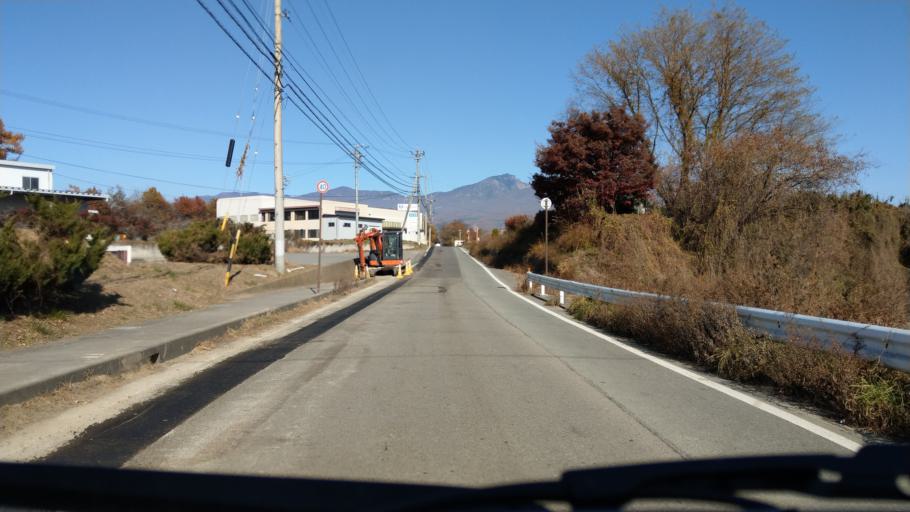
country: JP
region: Nagano
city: Komoro
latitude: 36.2927
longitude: 138.4860
